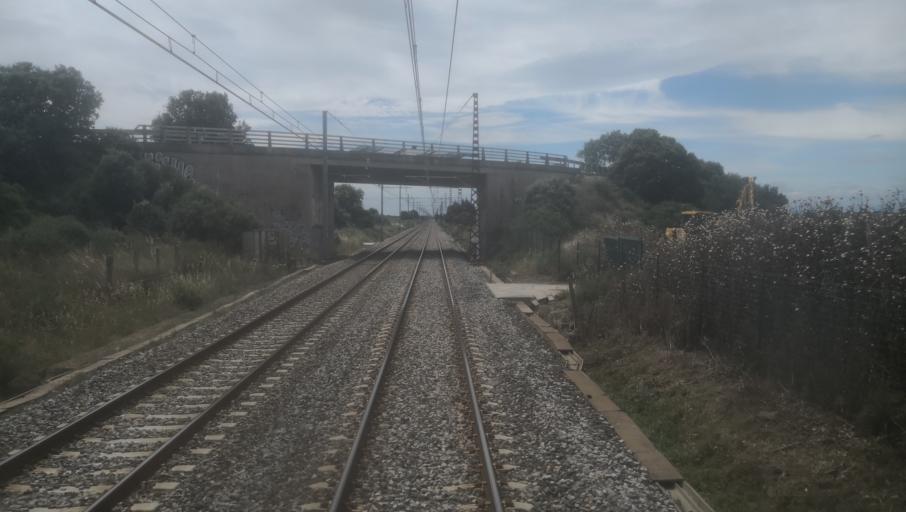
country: FR
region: Languedoc-Roussillon
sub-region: Departement de l'Herault
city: Portiragnes
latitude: 43.3195
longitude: 3.3607
